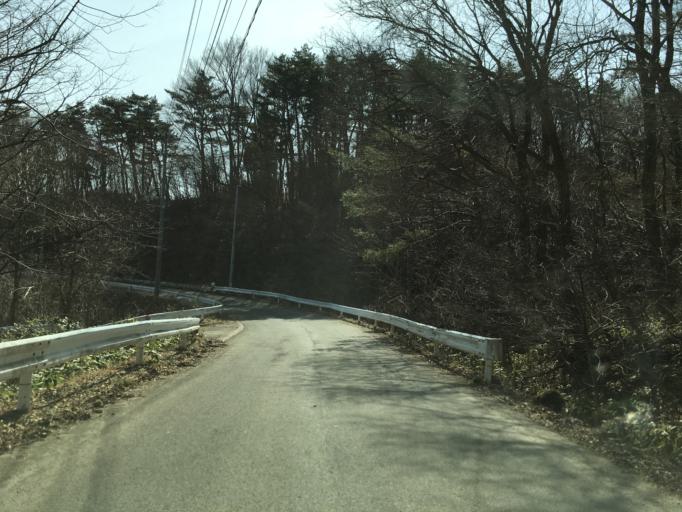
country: JP
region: Fukushima
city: Nihommatsu
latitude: 37.6363
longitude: 140.3579
